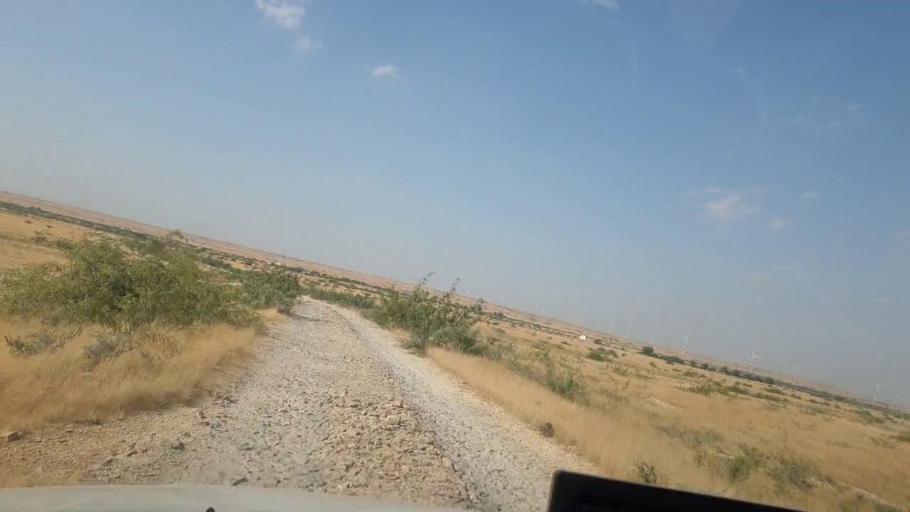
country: PK
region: Sindh
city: Daro Mehar
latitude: 25.0739
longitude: 68.0952
